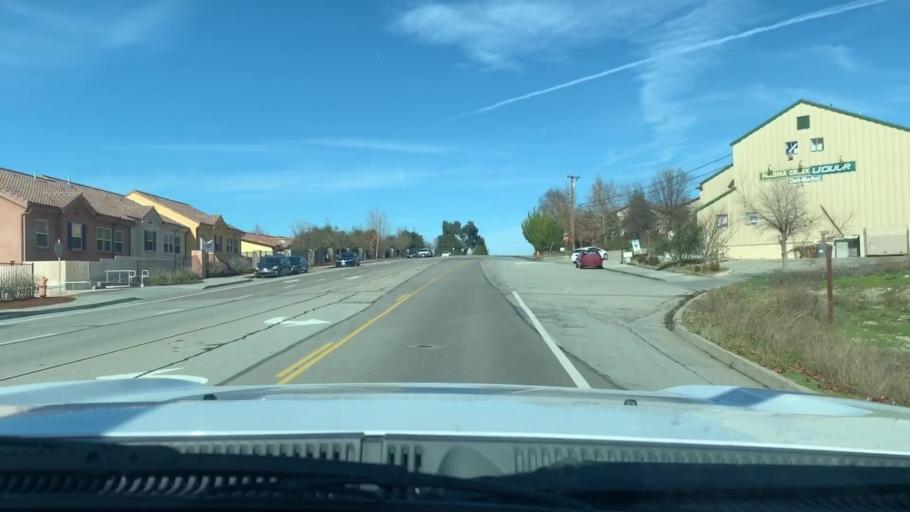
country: US
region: California
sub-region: San Luis Obispo County
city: Atascadero
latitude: 35.4541
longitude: -120.6389
